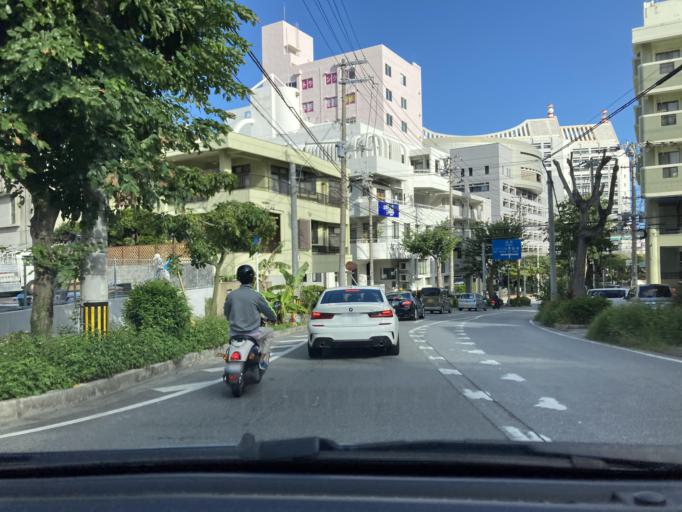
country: JP
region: Okinawa
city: Naha-shi
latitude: 26.2100
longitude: 127.6818
